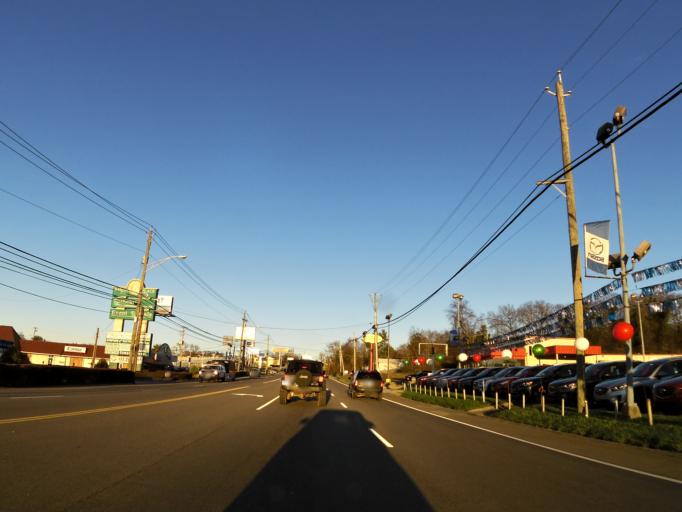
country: US
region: Tennessee
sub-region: Knox County
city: Farragut
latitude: 35.9160
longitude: -84.0754
